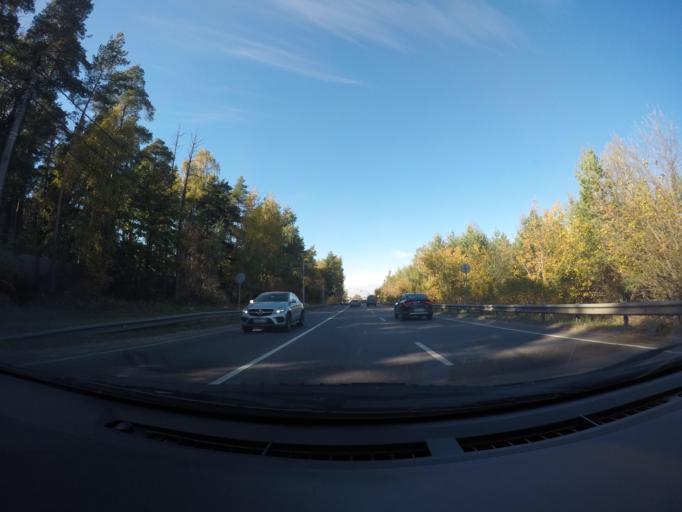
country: RU
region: Moskovskaya
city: Udel'naya
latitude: 55.6300
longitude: 37.9857
